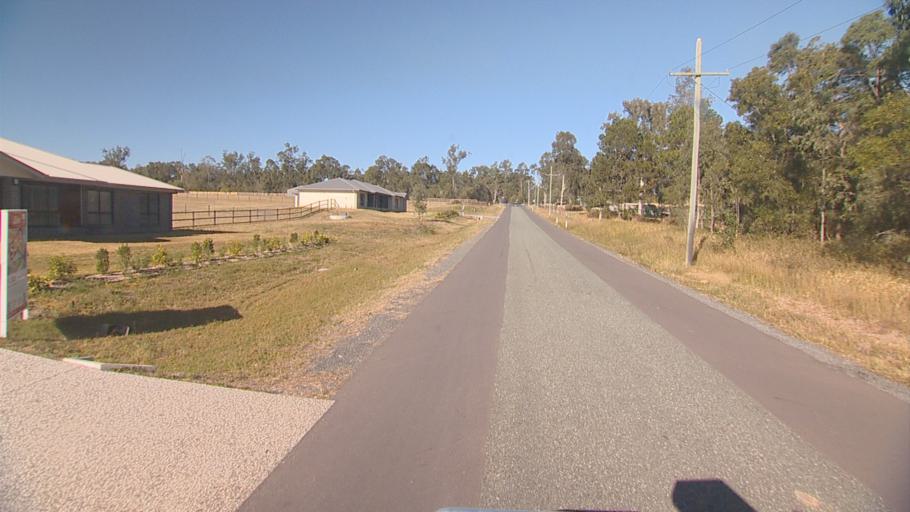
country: AU
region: Queensland
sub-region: Logan
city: North Maclean
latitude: -27.8127
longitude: 152.9925
